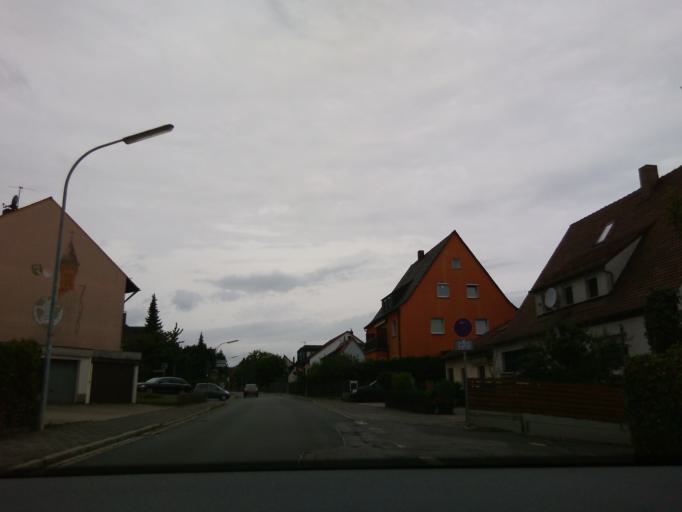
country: DE
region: Bavaria
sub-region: Regierungsbezirk Mittelfranken
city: Cadolzburg
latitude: 49.4594
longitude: 10.8633
